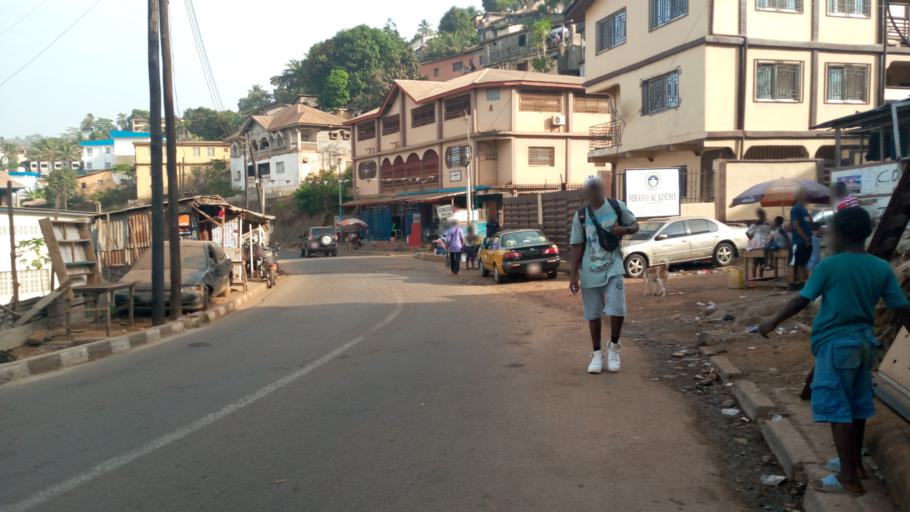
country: SL
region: Western Area
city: Freetown
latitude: 8.4756
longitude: -13.2586
